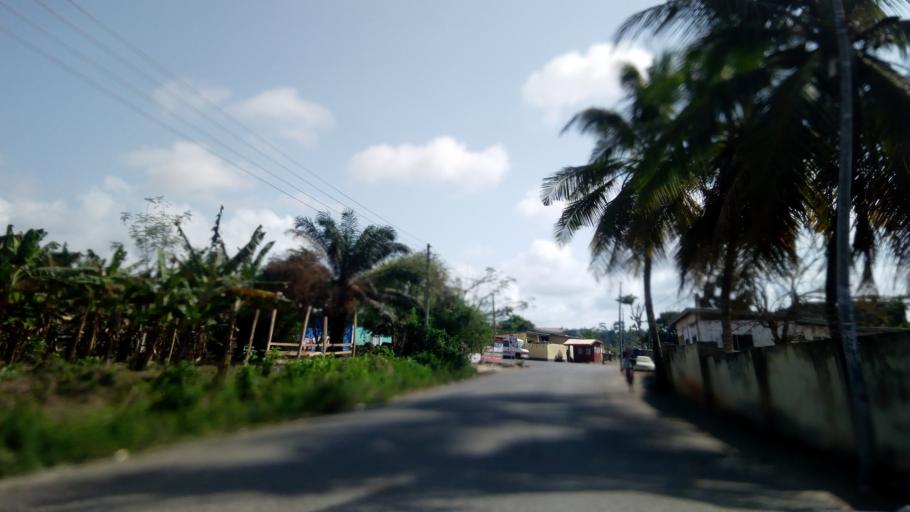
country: GH
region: Central
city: Cape Coast
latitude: 5.1159
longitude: -1.2676
